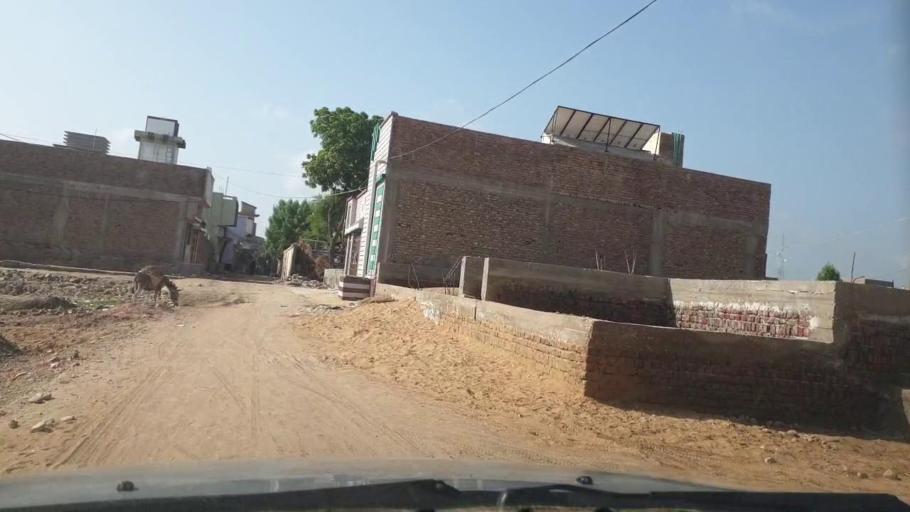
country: PK
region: Sindh
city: Matli
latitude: 25.0489
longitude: 68.6570
